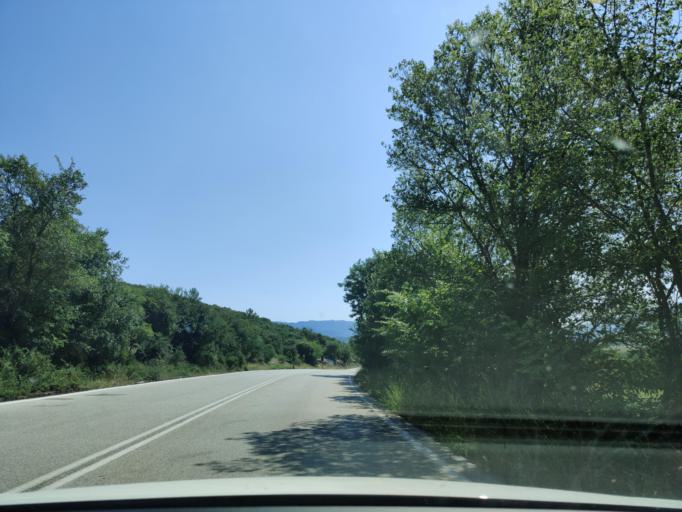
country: GR
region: East Macedonia and Thrace
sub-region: Nomos Kavalas
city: Zygos
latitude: 41.0050
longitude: 24.3818
